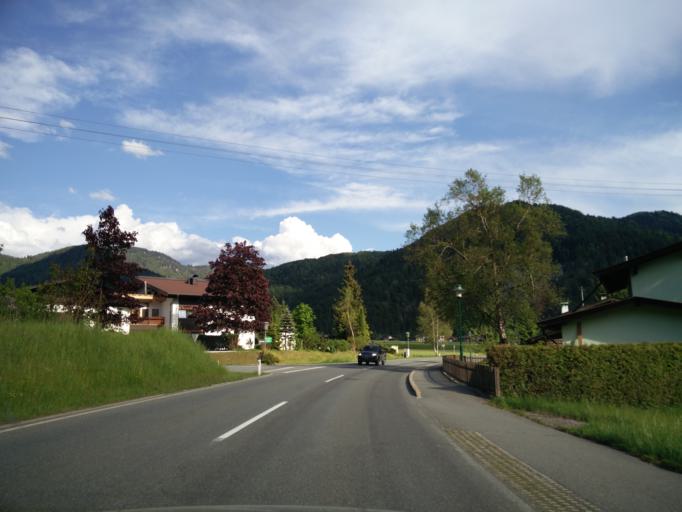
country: AT
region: Tyrol
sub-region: Politischer Bezirk Kitzbuhel
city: Kirchdorf in Tirol
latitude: 47.5820
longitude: 12.4765
